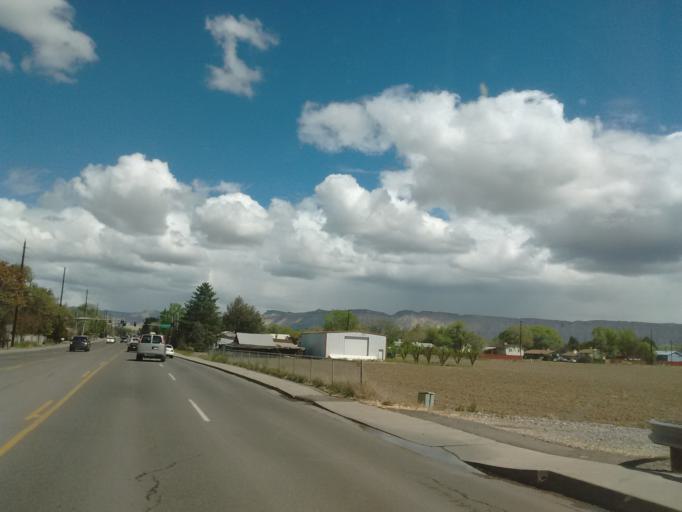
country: US
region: Colorado
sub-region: Mesa County
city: Fruitvale
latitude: 39.0830
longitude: -108.4965
